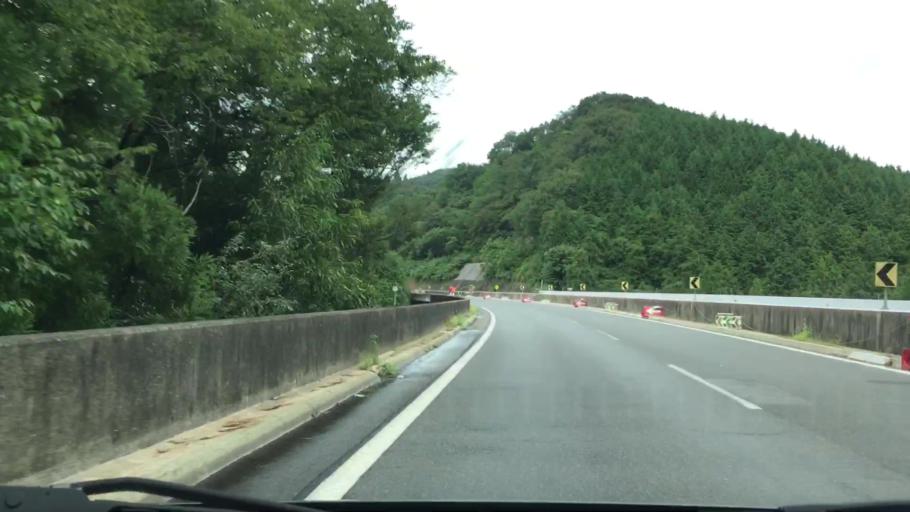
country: JP
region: Okayama
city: Niimi
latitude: 35.0171
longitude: 133.5838
